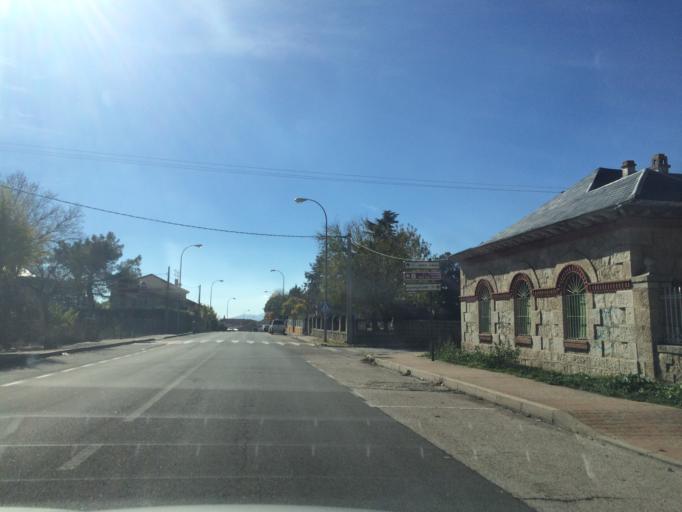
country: ES
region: Madrid
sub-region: Provincia de Madrid
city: La Cabrera
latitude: 40.8682
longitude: -3.6108
